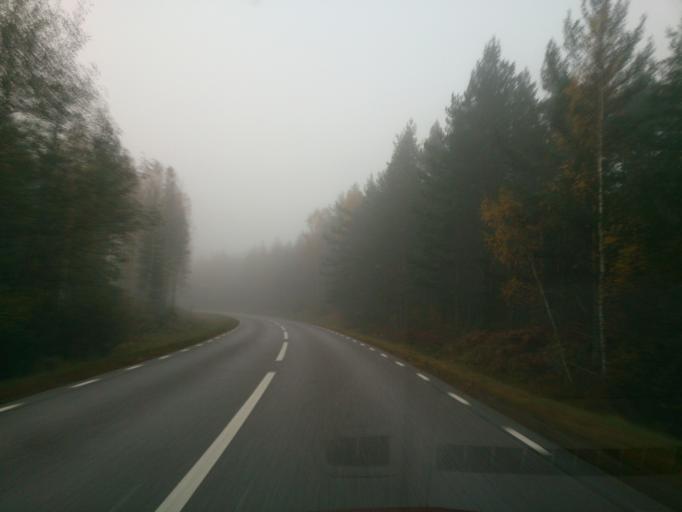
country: SE
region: OEstergoetland
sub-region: Atvidabergs Kommun
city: Atvidaberg
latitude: 58.0957
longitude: 15.9429
